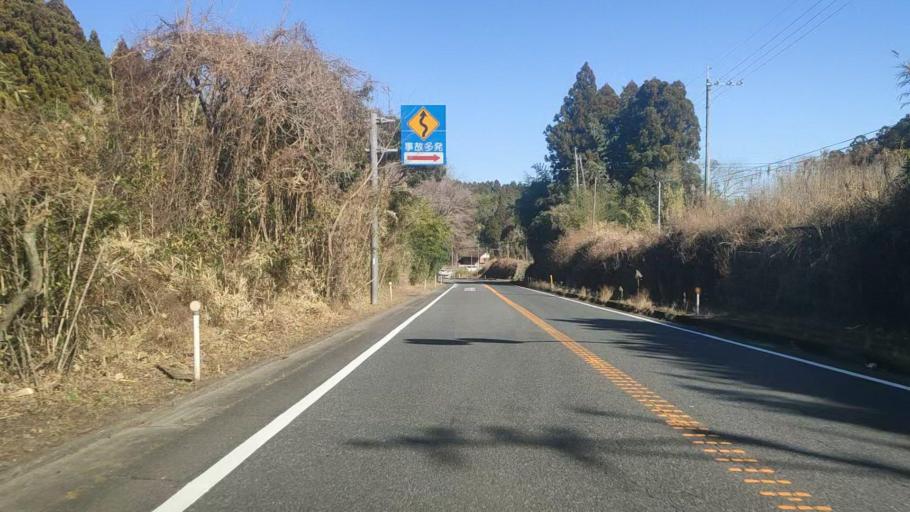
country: JP
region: Kagoshima
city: Sueyoshicho-ninokata
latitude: 31.6920
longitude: 130.9722
